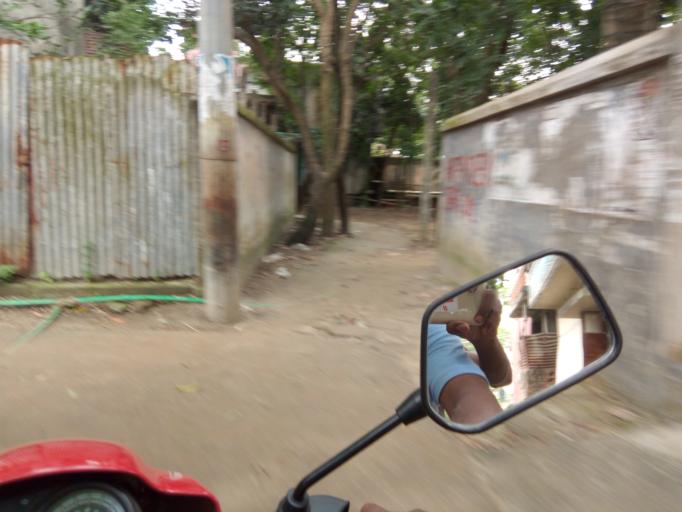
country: BD
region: Dhaka
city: Paltan
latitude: 23.7372
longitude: 90.4760
